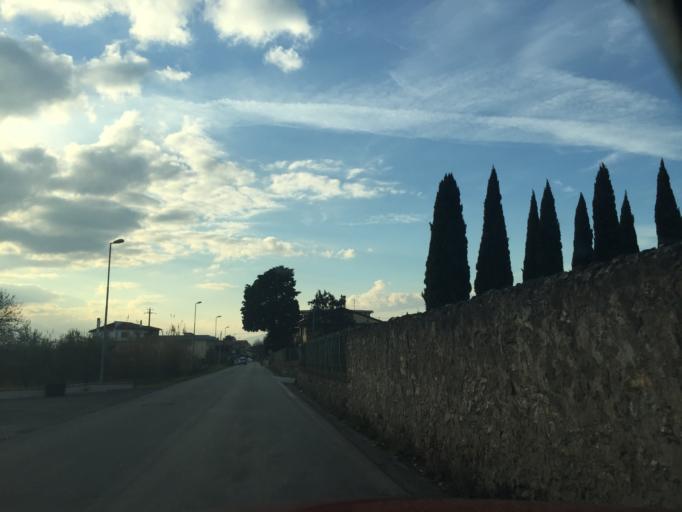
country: IT
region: Tuscany
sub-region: Provincia di Pistoia
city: Cintolese
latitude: 43.8595
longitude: 10.8279
